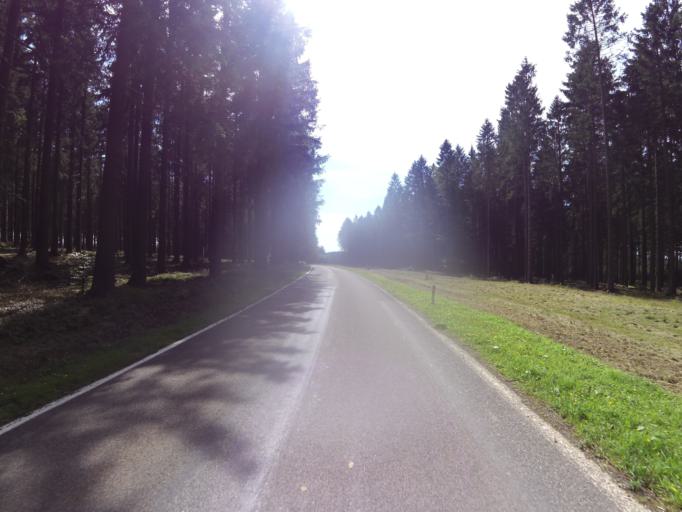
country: BE
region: Wallonia
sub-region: Province du Luxembourg
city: Saint-Hubert
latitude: 50.0535
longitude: 5.3463
